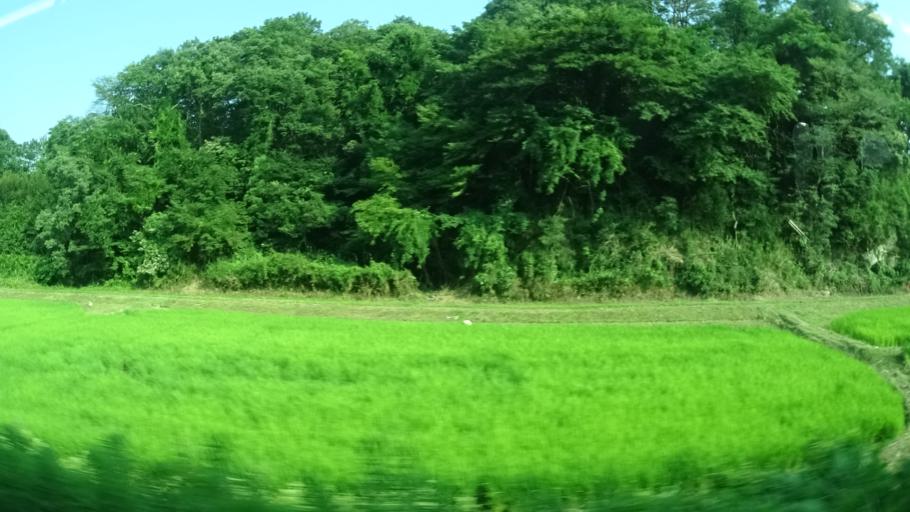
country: JP
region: Fukushima
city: Iwaki
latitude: 36.9498
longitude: 140.8383
